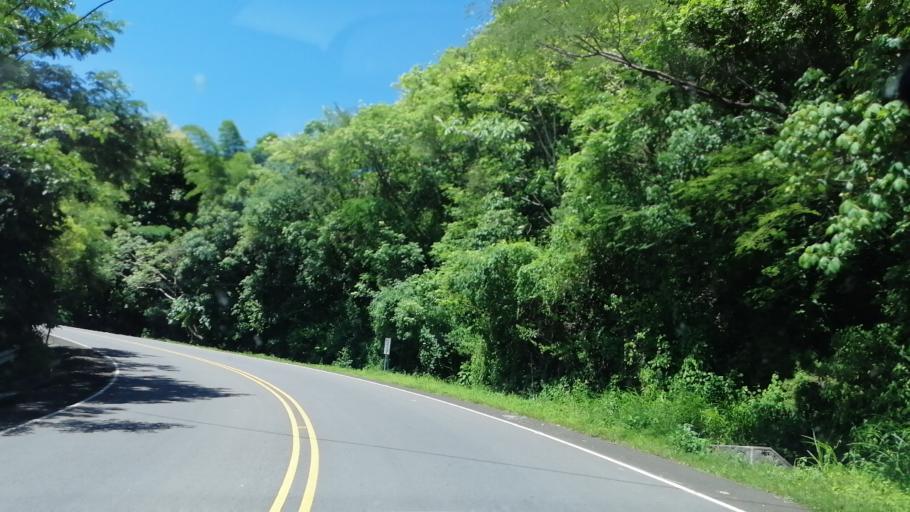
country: SV
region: San Miguel
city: Ciudad Barrios
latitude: 13.8123
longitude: -88.1765
